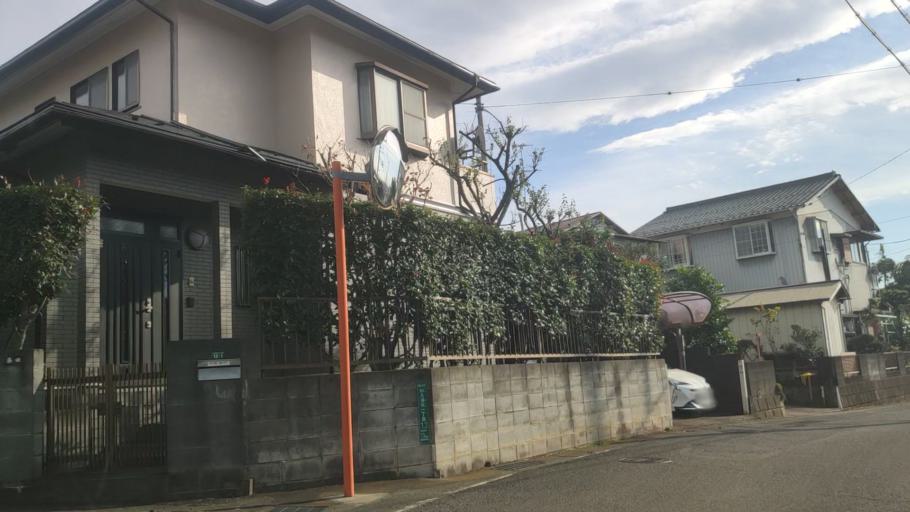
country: JP
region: Kanagawa
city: Atsugi
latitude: 35.4303
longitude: 139.3968
